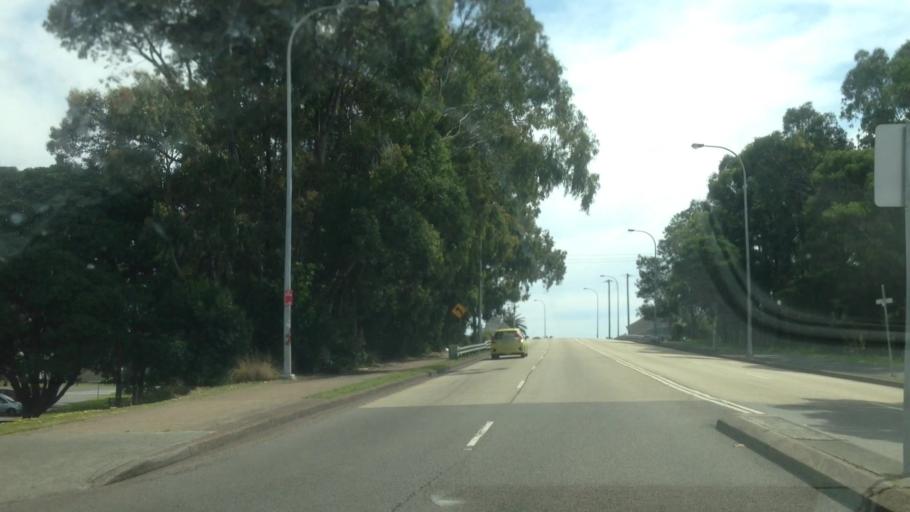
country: AU
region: New South Wales
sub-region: Newcastle
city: Broadmeadow
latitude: -32.9244
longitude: 151.7351
